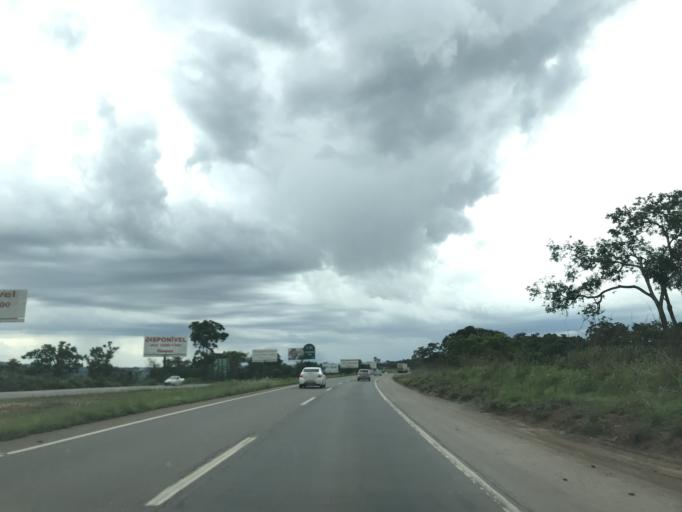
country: BR
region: Goias
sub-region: Hidrolandia
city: Hidrolandia
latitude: -16.9164
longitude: -49.2531
